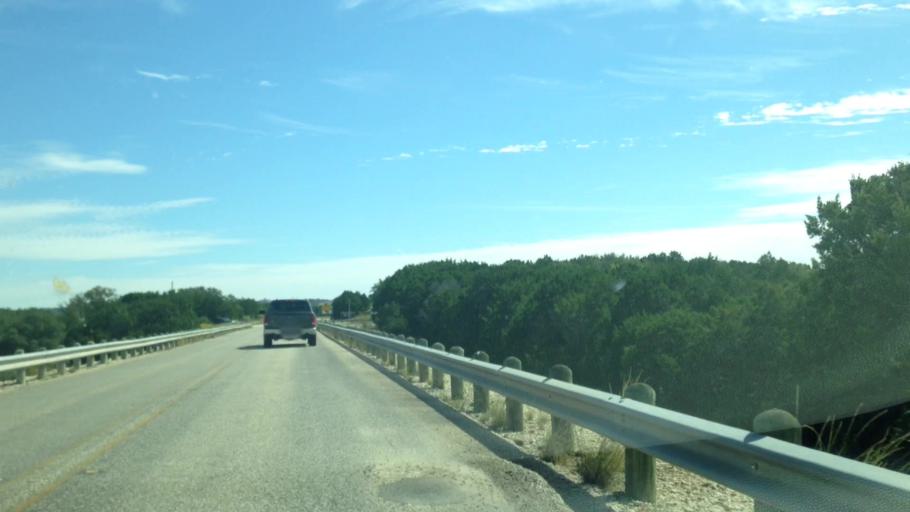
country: US
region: Texas
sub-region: Travis County
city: Hudson Bend
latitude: 30.3965
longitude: -97.9117
